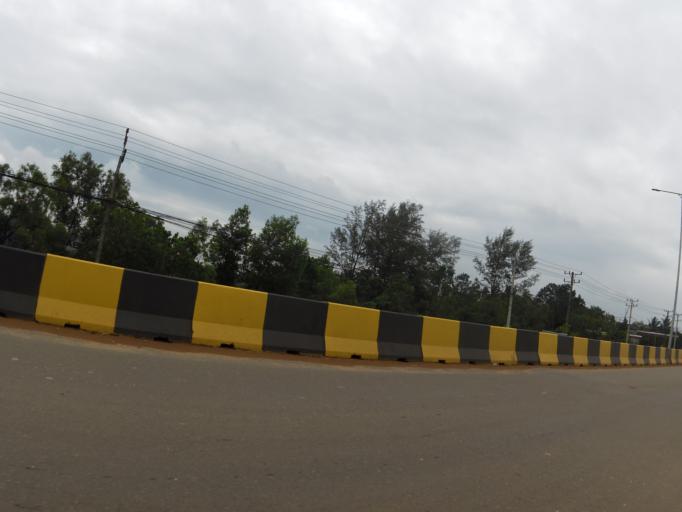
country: KH
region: Preah Sihanouk
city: Sihanoukville
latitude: 10.6363
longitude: 103.5333
